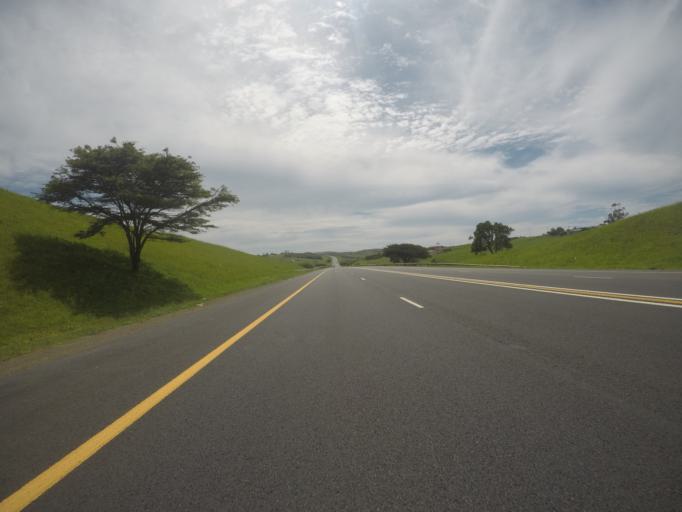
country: ZA
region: KwaZulu-Natal
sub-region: iLembe District Municipality
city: Mandeni
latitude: -29.1727
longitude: 31.5150
